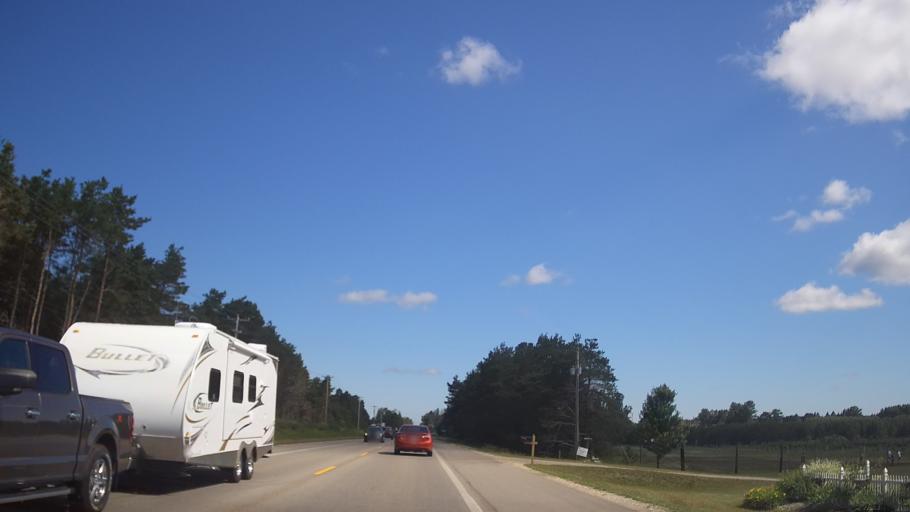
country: US
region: Michigan
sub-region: Cheboygan County
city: Indian River
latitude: 45.4880
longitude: -84.7812
